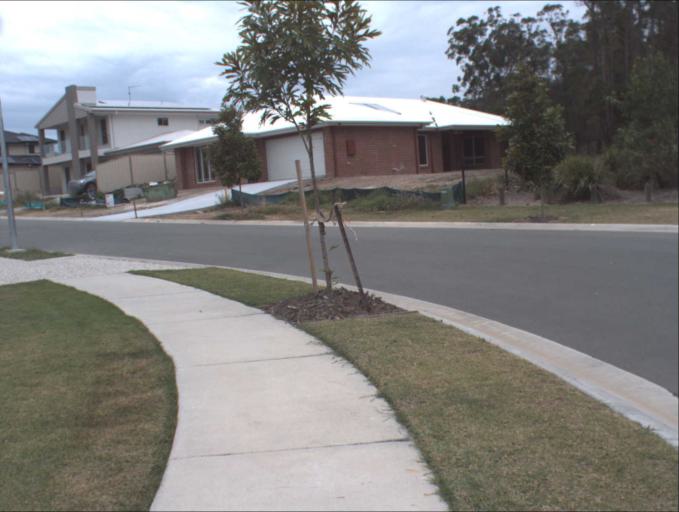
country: AU
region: Queensland
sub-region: Logan
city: Slacks Creek
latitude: -27.6578
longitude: 153.2030
